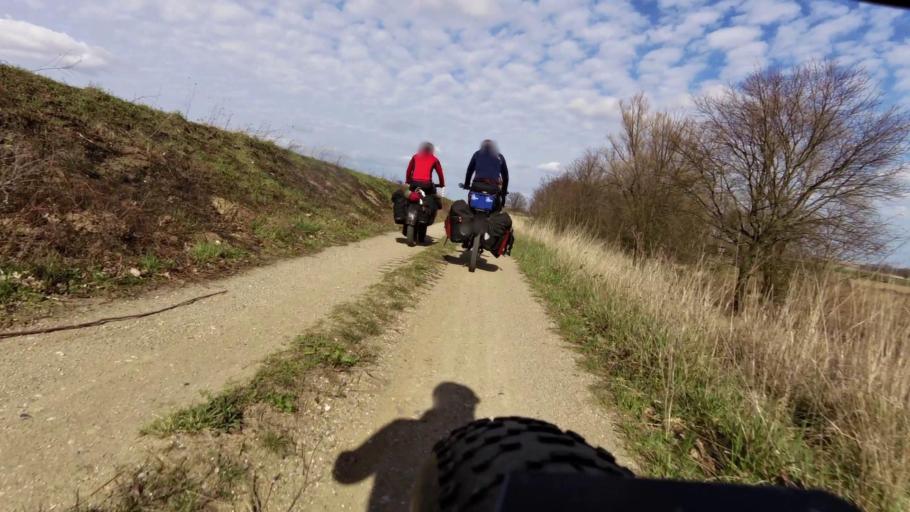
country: DE
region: Brandenburg
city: Reitwein
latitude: 52.4557
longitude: 14.6016
